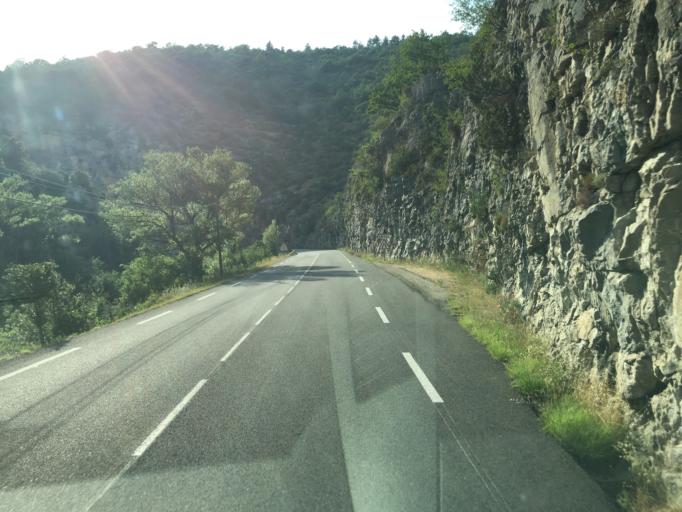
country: FR
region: Rhone-Alpes
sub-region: Departement de la Drome
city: Buis-les-Baronnies
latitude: 44.4323
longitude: 5.2851
